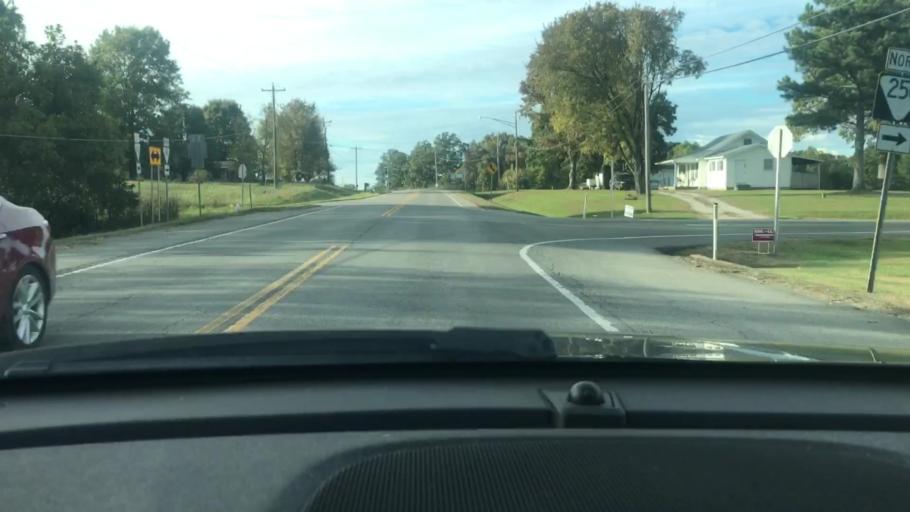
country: US
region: Tennessee
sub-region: Dickson County
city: White Bluff
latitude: 36.1374
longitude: -87.2392
